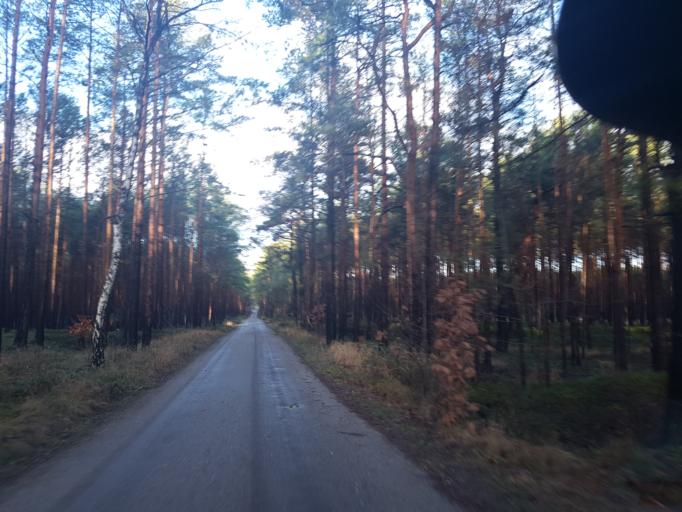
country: DE
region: Brandenburg
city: Ruckersdorf
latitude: 51.5856
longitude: 13.5979
